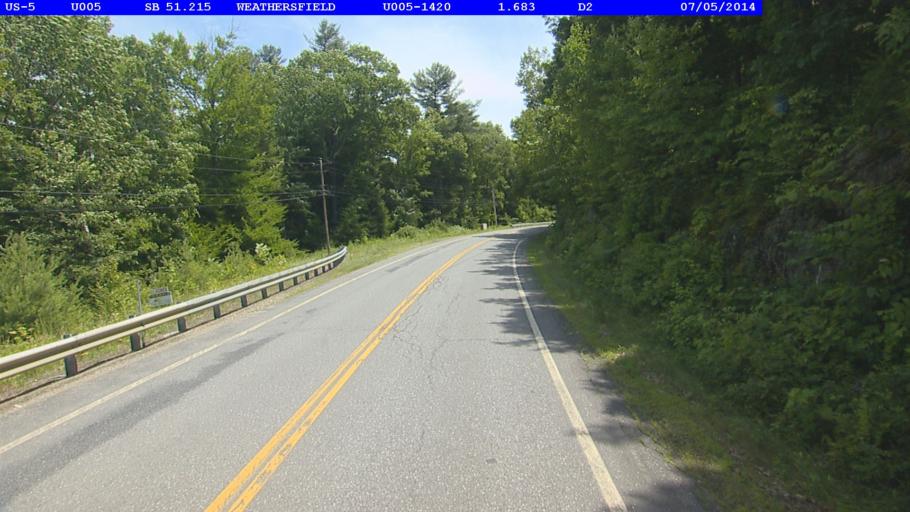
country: US
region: New Hampshire
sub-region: Sullivan County
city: Claremont
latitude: 43.3614
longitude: -72.4112
